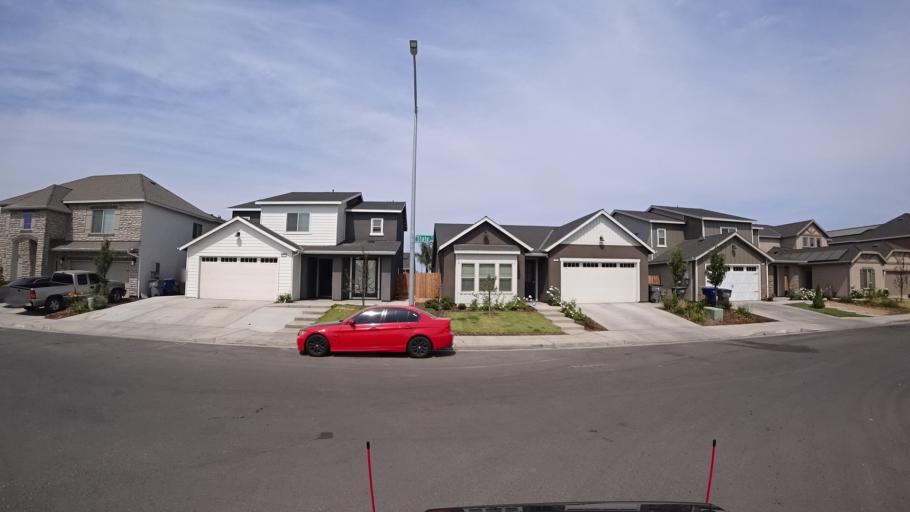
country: US
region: California
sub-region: Fresno County
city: West Park
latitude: 36.7598
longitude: -119.8864
